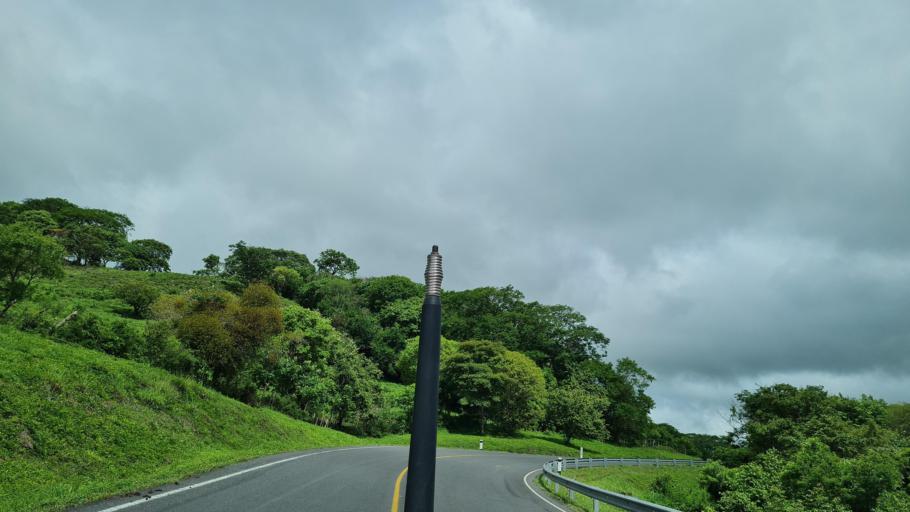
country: NI
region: Matagalpa
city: Terrabona
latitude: 12.5921
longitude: -85.9194
